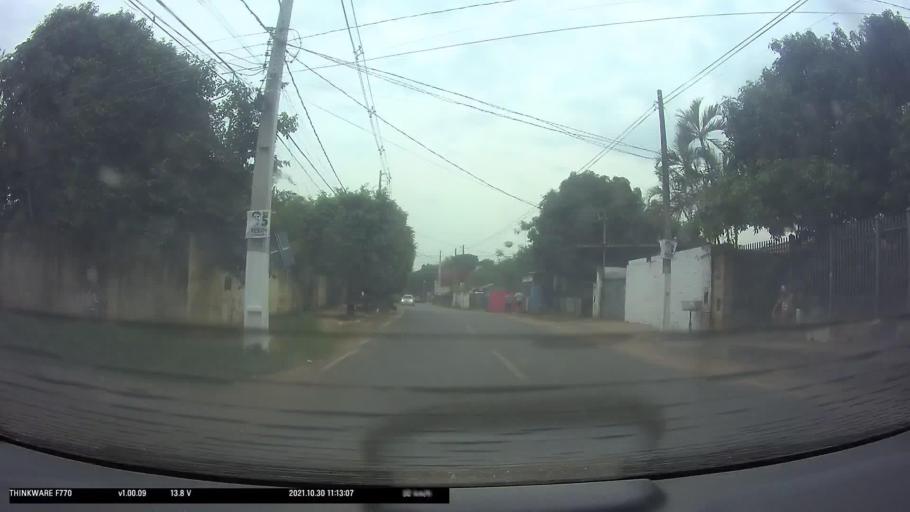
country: PY
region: Central
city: San Lorenzo
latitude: -25.3096
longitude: -57.5081
